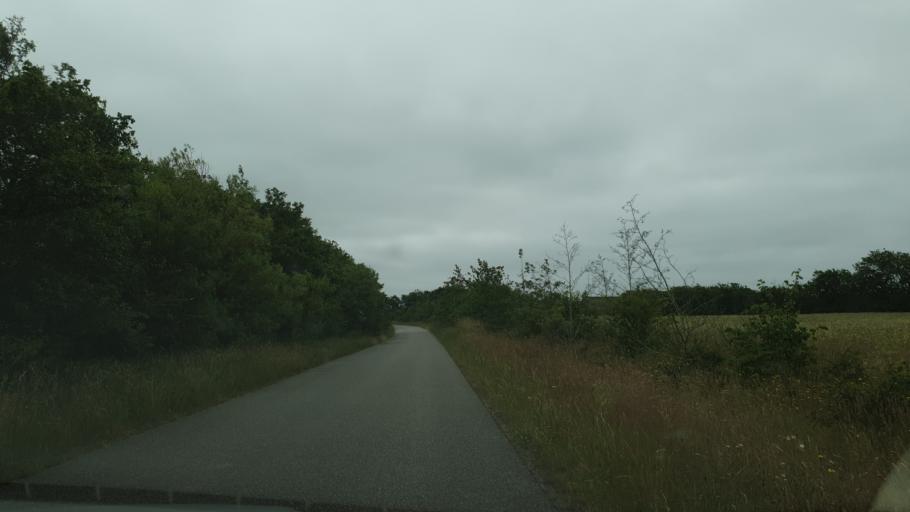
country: DK
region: Central Jutland
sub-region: Ringkobing-Skjern Kommune
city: Skjern
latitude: 55.9439
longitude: 8.4000
